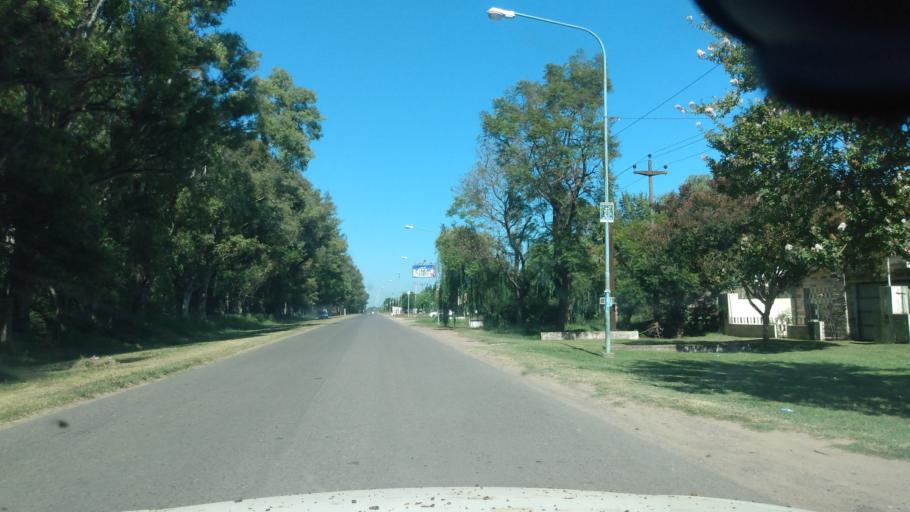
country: AR
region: Buenos Aires
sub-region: Partido de Lujan
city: Lujan
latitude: -34.5026
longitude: -59.0723
